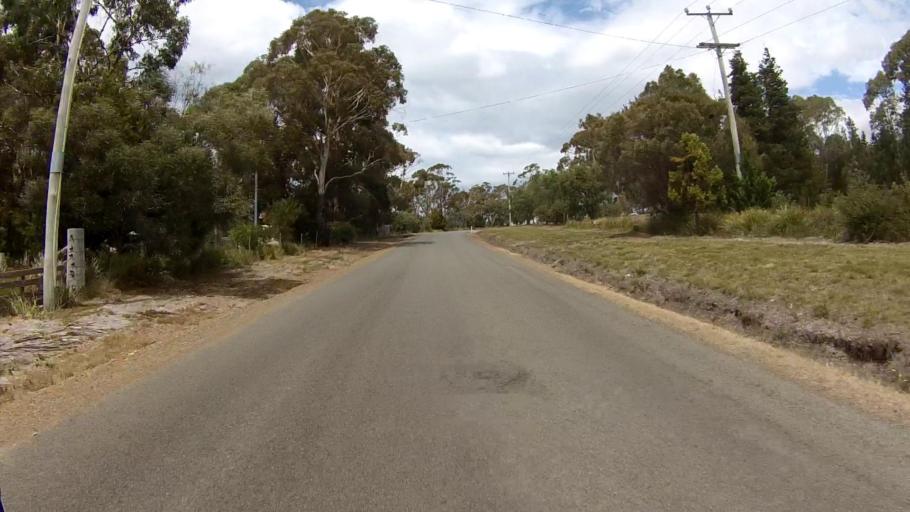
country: AU
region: Tasmania
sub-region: Sorell
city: Sorell
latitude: -42.5855
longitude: 147.9138
